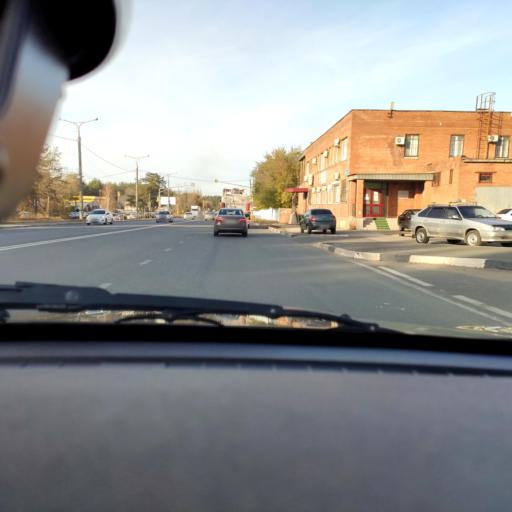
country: RU
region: Samara
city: Zhigulevsk
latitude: 53.4951
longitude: 49.4737
